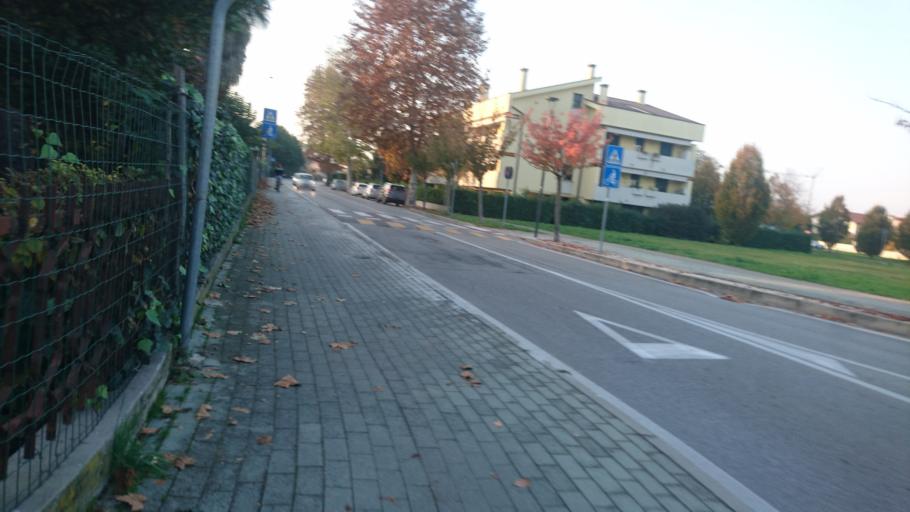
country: IT
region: Veneto
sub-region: Provincia di Padova
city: Montegrotto Terme
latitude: 45.3394
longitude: 11.7874
